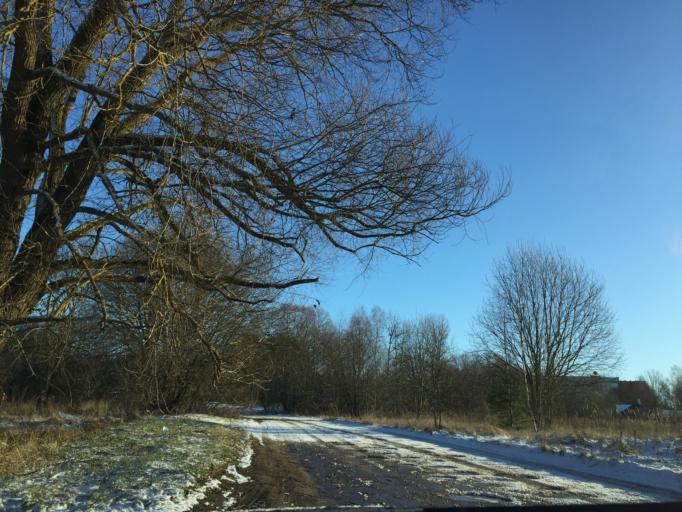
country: LV
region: Kekava
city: Balozi
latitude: 56.9086
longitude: 24.1374
